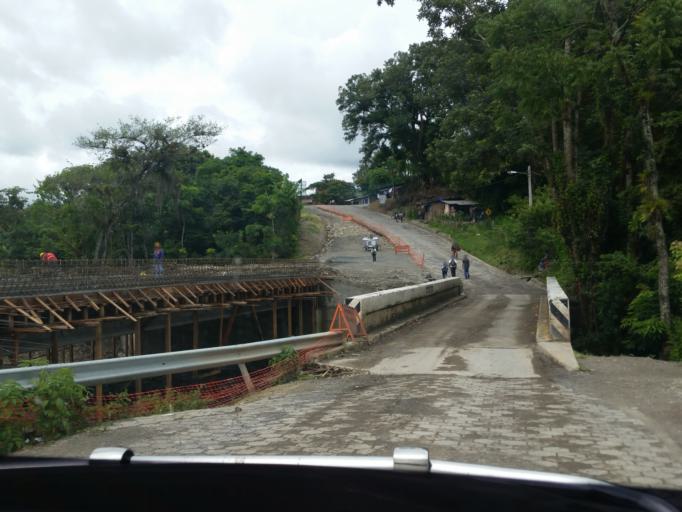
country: NI
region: Jinotega
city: Jinotega
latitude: 13.1796
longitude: -85.9111
